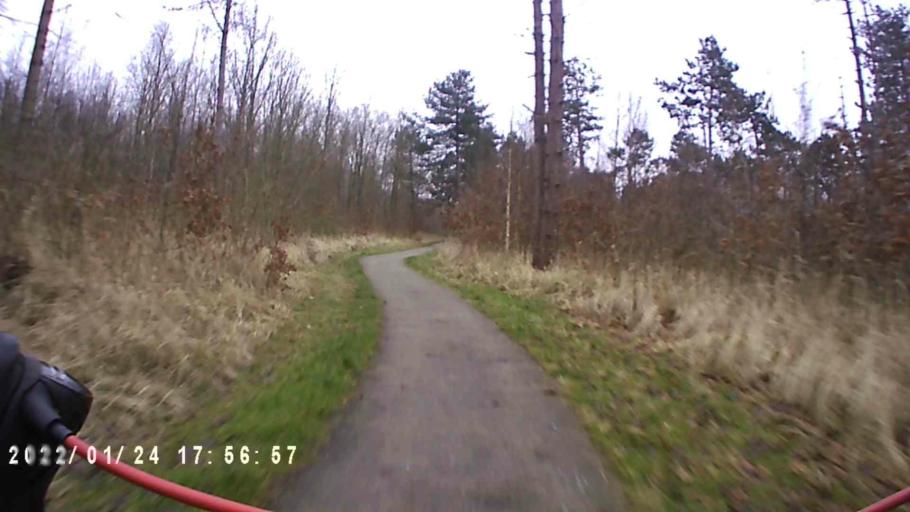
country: NL
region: Groningen
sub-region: Gemeente De Marne
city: Ulrum
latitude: 53.3981
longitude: 6.2359
